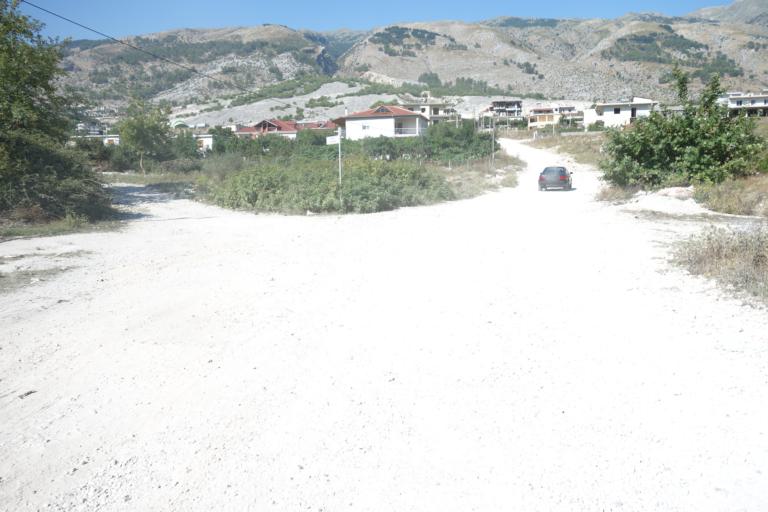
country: AL
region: Gjirokaster
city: Gjirokaster
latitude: 40.0876
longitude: 20.1363
